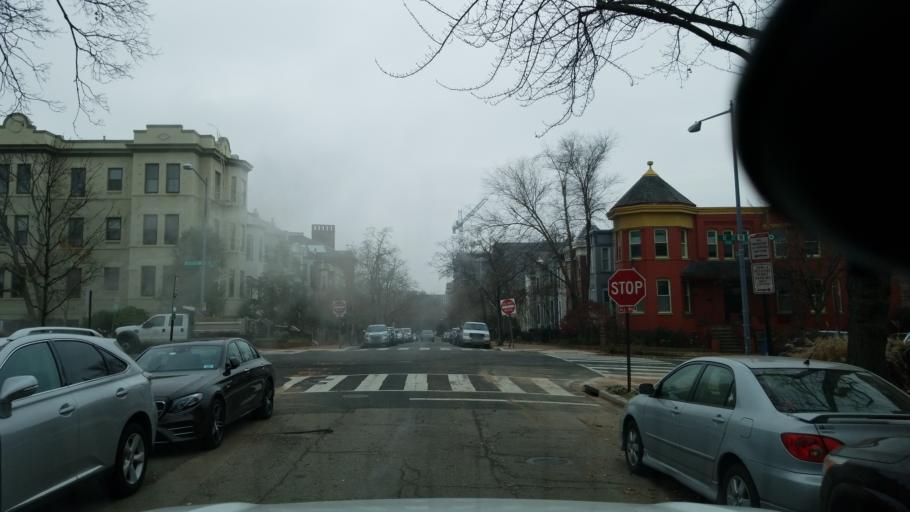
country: US
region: Washington, D.C.
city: Washington, D.C.
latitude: 38.8836
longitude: -77.0036
